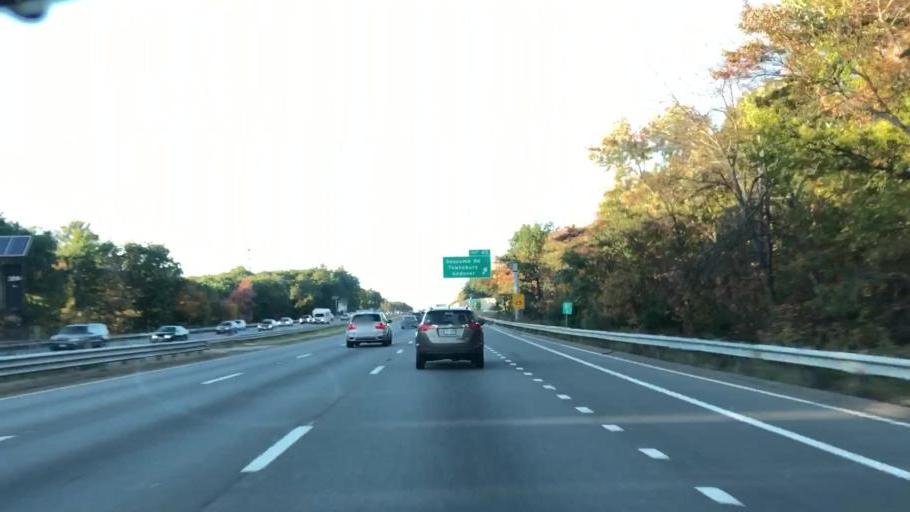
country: US
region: Massachusetts
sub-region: Essex County
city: Andover
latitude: 42.6207
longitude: -71.1765
